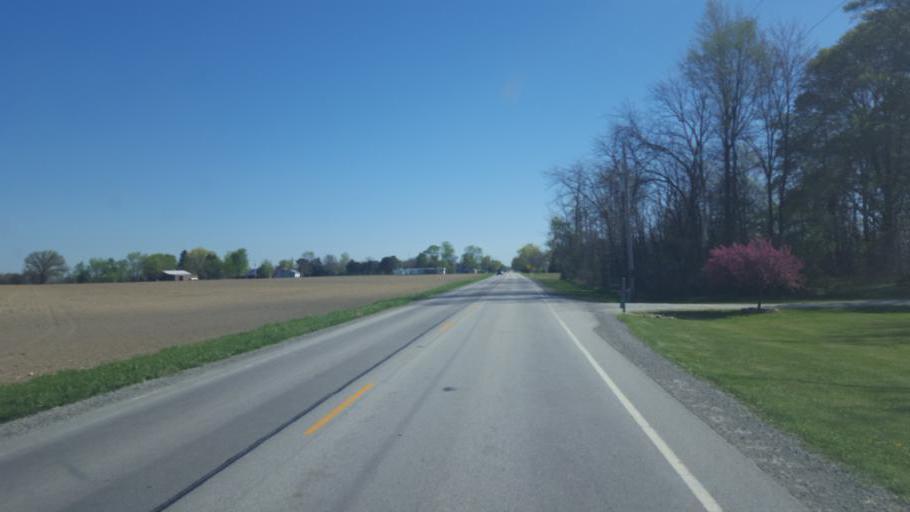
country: US
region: Ohio
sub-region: Wyandot County
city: Upper Sandusky
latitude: 40.9235
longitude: -83.2041
